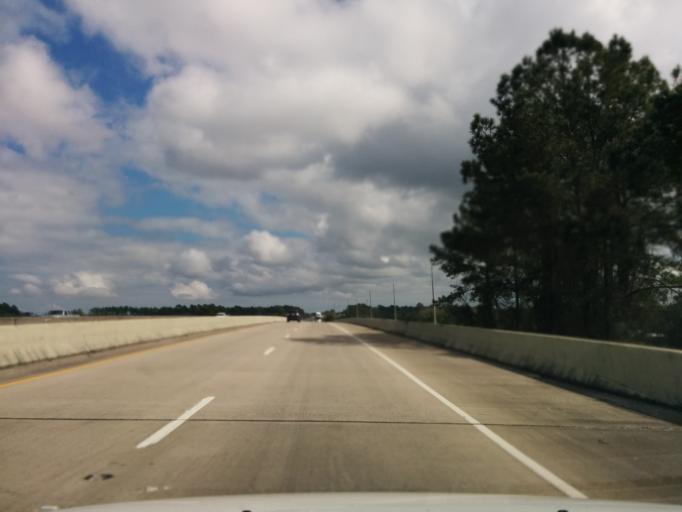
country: US
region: Georgia
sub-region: Glynn County
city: Brunswick
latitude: 31.1277
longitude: -81.5536
